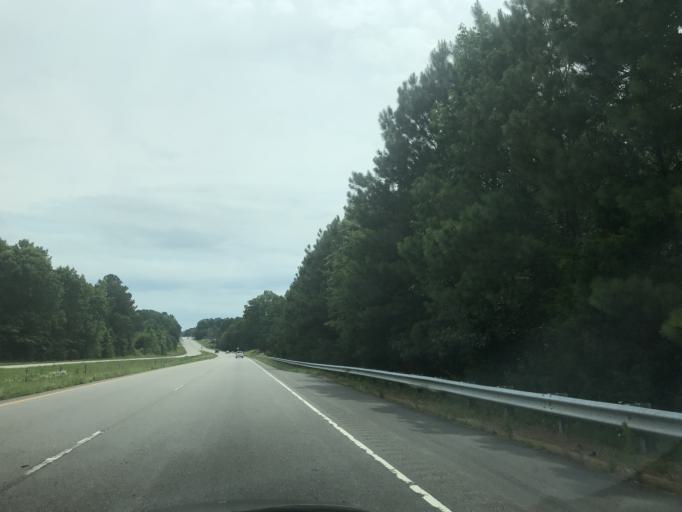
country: US
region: North Carolina
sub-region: Vance County
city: South Henderson
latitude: 36.2316
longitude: -78.4404
